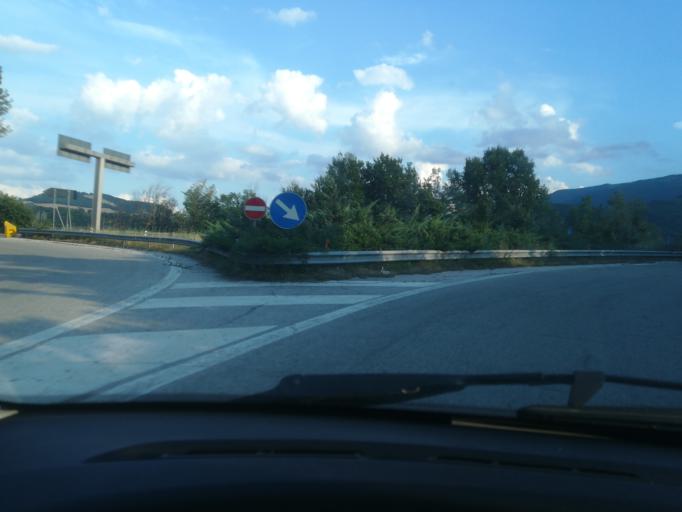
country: IT
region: The Marches
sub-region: Provincia di Macerata
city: Caldarola
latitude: 43.1516
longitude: 13.2174
